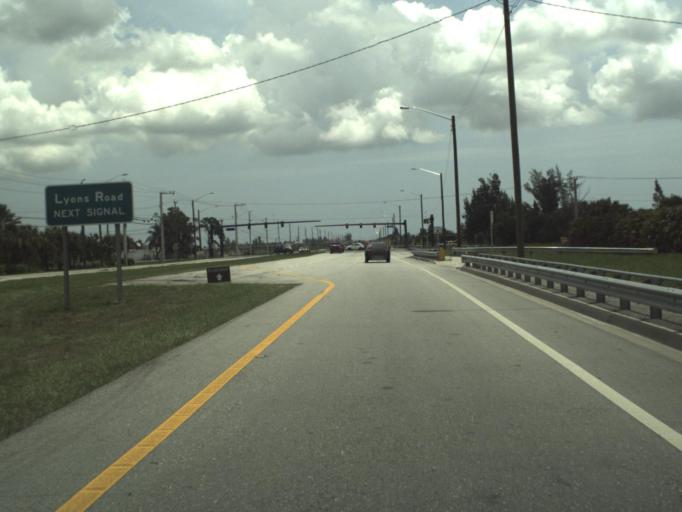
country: US
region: Florida
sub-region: Palm Beach County
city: Villages of Oriole
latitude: 26.4536
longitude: -80.1898
